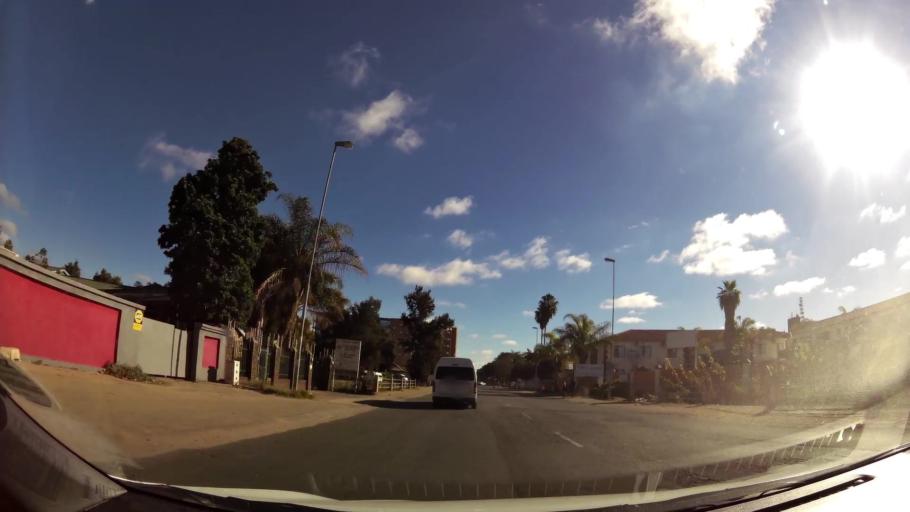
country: ZA
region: Limpopo
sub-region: Capricorn District Municipality
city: Polokwane
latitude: -23.9160
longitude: 29.4512
